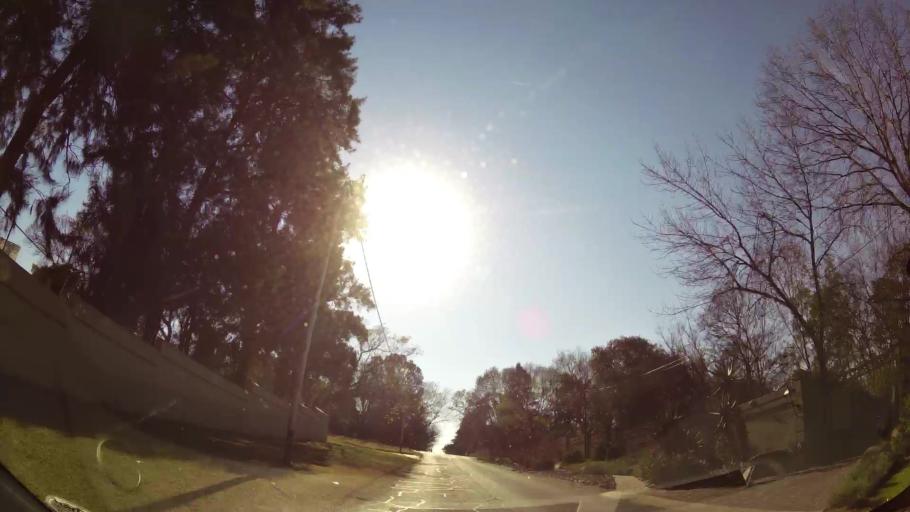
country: ZA
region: Gauteng
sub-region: City of Johannesburg Metropolitan Municipality
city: Midrand
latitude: -26.0589
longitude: 28.0433
